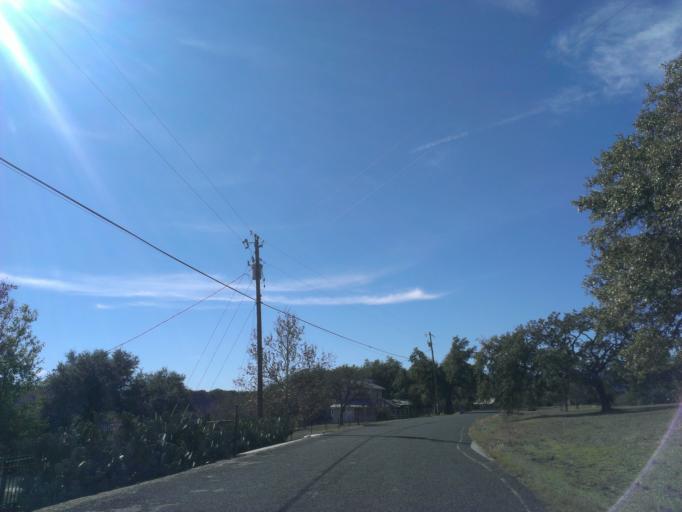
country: US
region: Texas
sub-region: Travis County
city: Briarcliff
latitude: 30.4313
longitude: -98.0639
